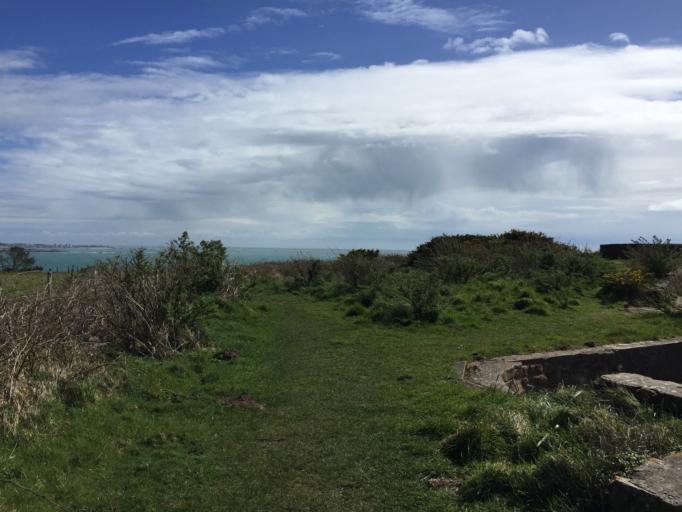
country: JE
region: St Helier
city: Saint Helier
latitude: 49.1691
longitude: -2.1687
